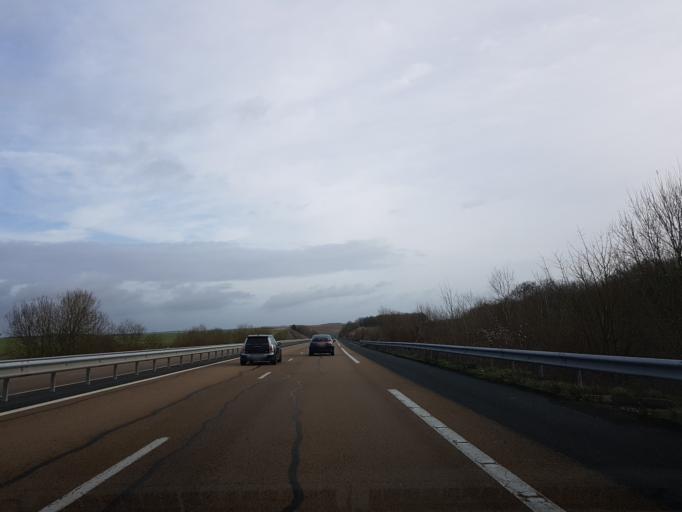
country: FR
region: Champagne-Ardenne
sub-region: Departement de l'Aube
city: Aix-en-Othe
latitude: 48.2687
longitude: 3.6992
